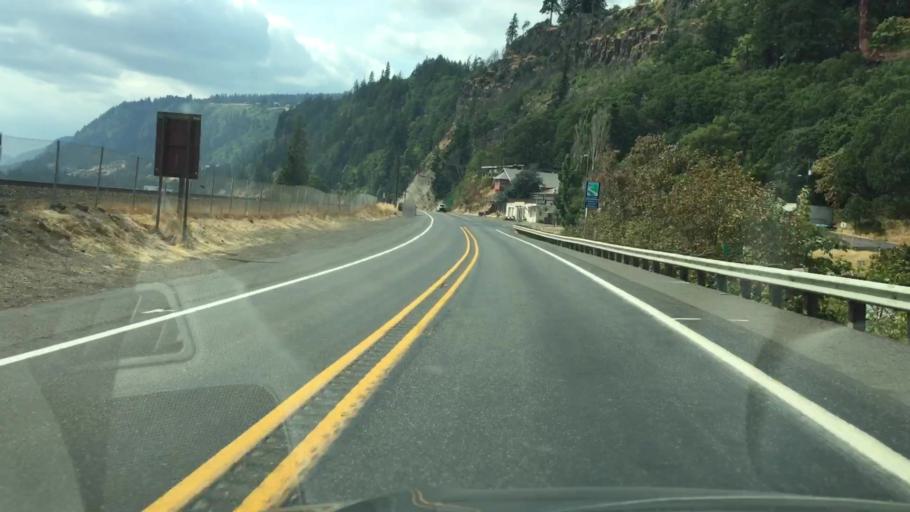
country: US
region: Oregon
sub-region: Hood River County
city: Hood River
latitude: 45.7290
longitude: -121.5235
